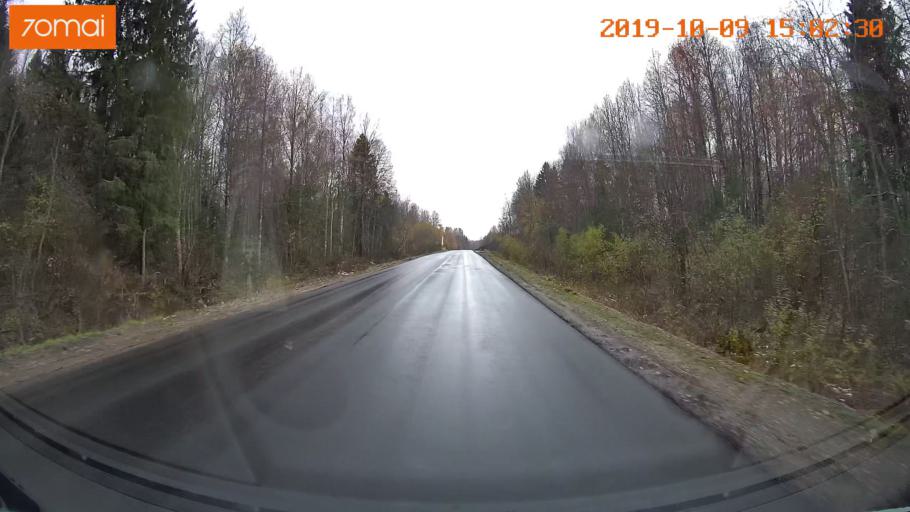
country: RU
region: Kostroma
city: Chistyye Bory
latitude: 58.2842
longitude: 41.6787
